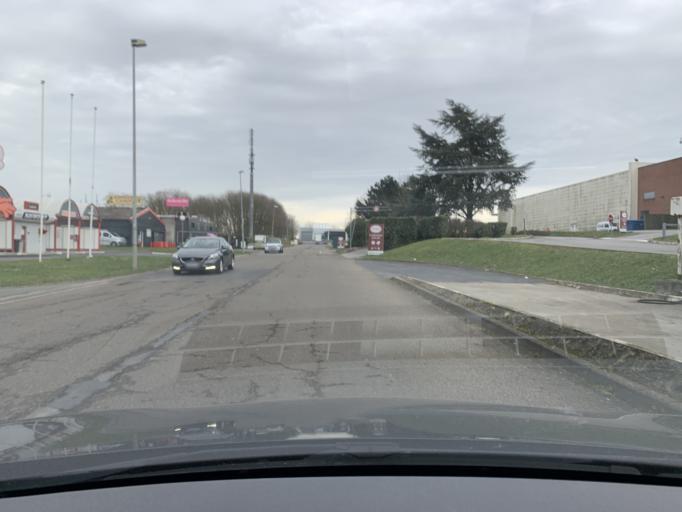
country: FR
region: Nord-Pas-de-Calais
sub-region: Departement du Nord
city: Proville
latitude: 50.1489
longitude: 3.2223
